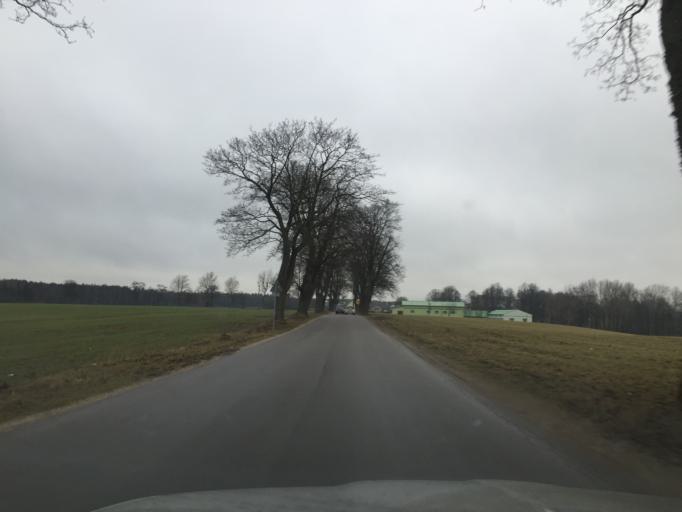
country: PL
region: Pomeranian Voivodeship
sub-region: Powiat kartuski
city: Banino
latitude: 54.4021
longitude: 18.4323
